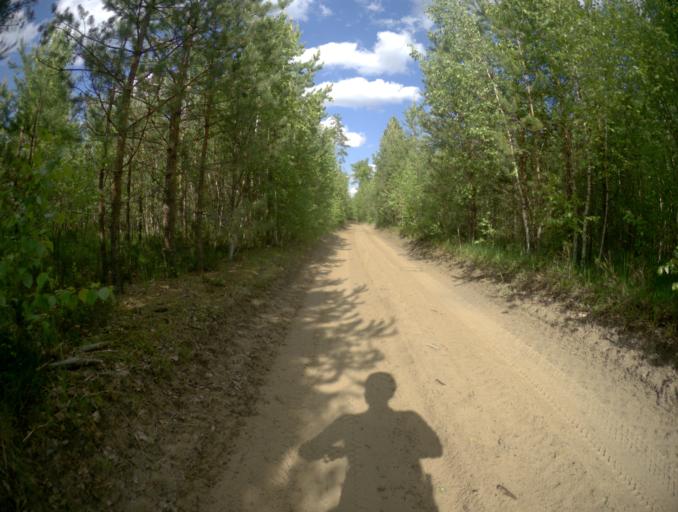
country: RU
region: Vladimir
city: Zolotkovo
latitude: 55.3307
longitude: 40.9831
